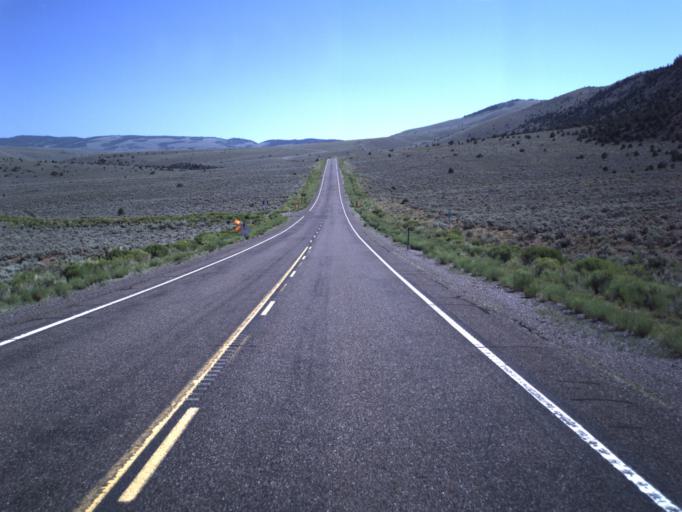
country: US
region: Utah
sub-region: Wayne County
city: Loa
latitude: 38.5181
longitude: -111.5226
